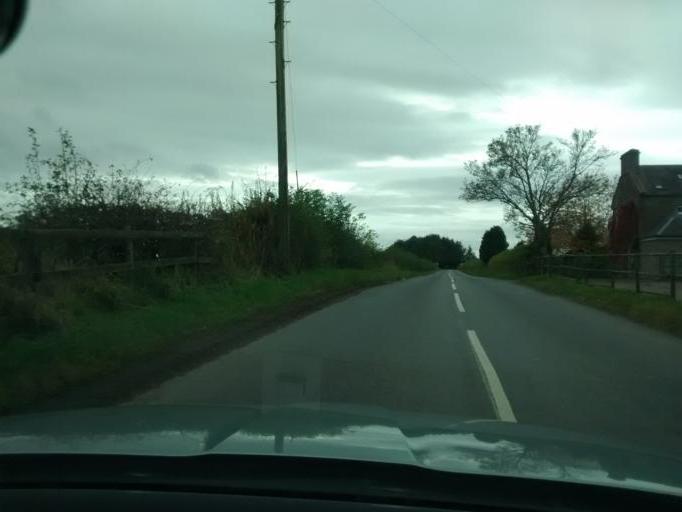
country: GB
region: Scotland
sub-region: Perth and Kinross
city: Stanley
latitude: 56.5068
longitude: -3.4154
